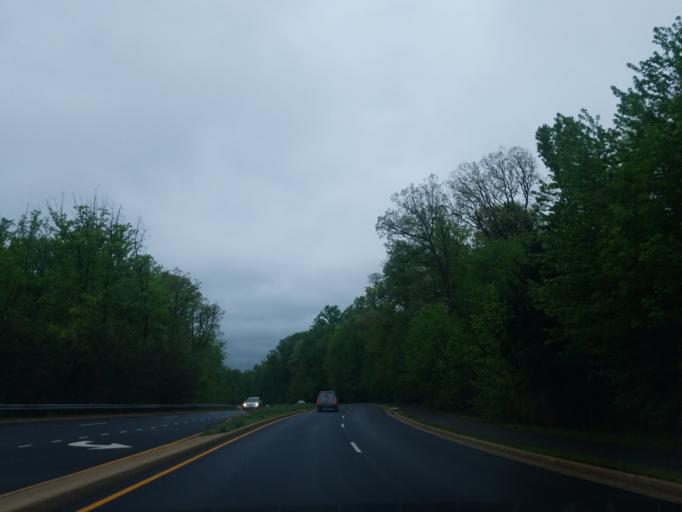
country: US
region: Virginia
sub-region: Fairfax County
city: Dranesville
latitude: 38.9874
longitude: -77.3464
